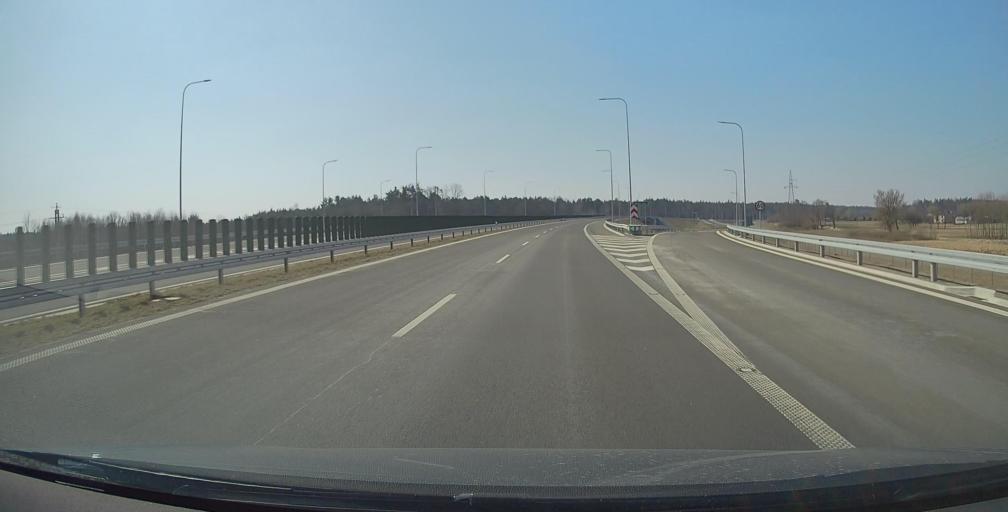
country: PL
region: Lublin Voivodeship
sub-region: Powiat janowski
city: Janow Lubelski
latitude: 50.6957
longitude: 22.3777
